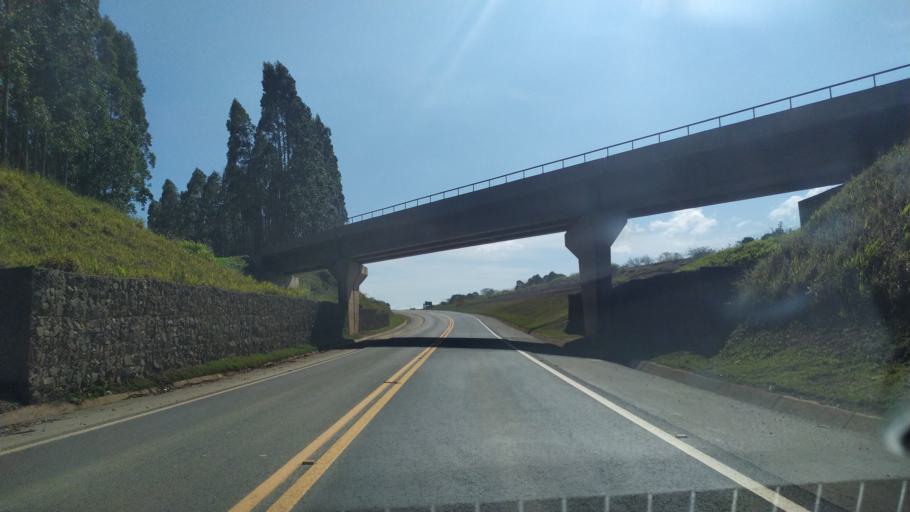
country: BR
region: Parana
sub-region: Telemaco Borba
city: Telemaco Borba
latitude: -24.2470
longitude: -50.7524
